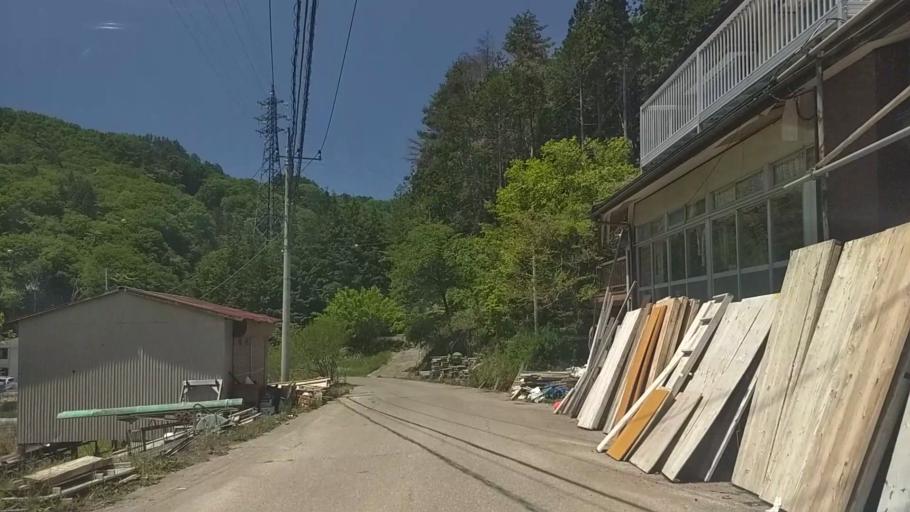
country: JP
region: Yamanashi
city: Nirasaki
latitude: 35.8769
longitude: 138.4309
